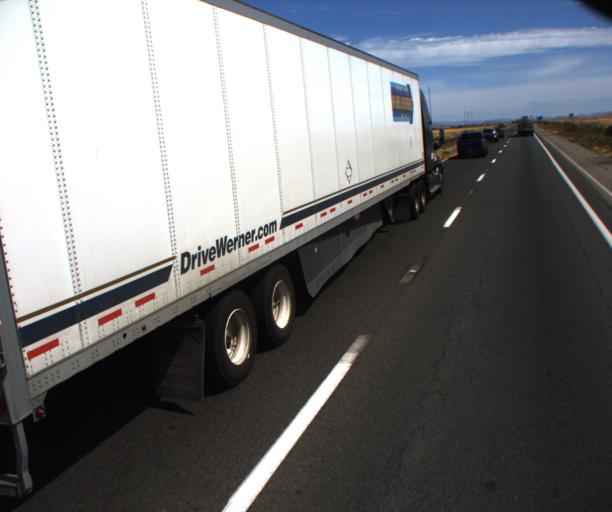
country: US
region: Arizona
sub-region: Yavapai County
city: Black Canyon City
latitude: 34.1710
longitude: -112.1361
